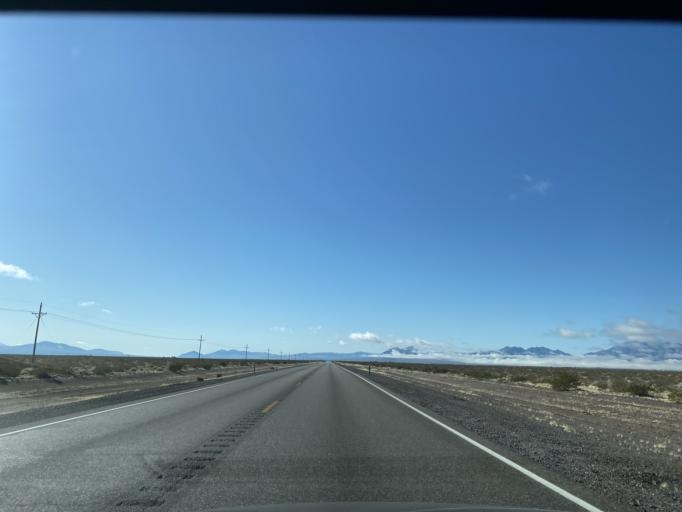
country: US
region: Nevada
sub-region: Nye County
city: Beatty
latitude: 36.6017
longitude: -116.4078
